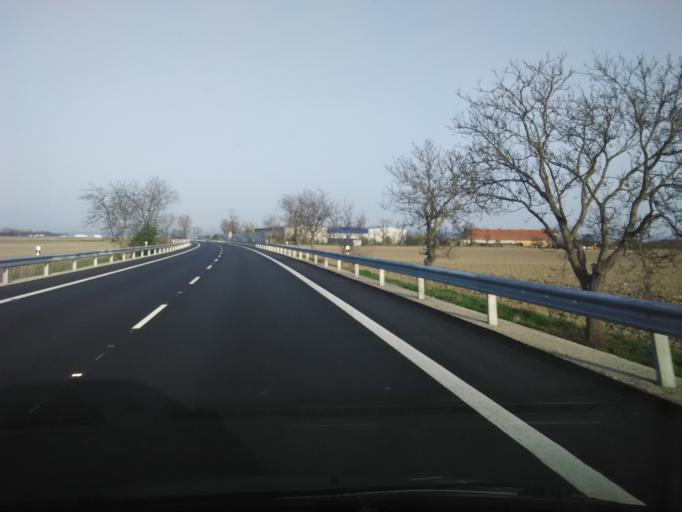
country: SK
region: Trnavsky
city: Sladkovicovo
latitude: 48.2012
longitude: 17.5584
